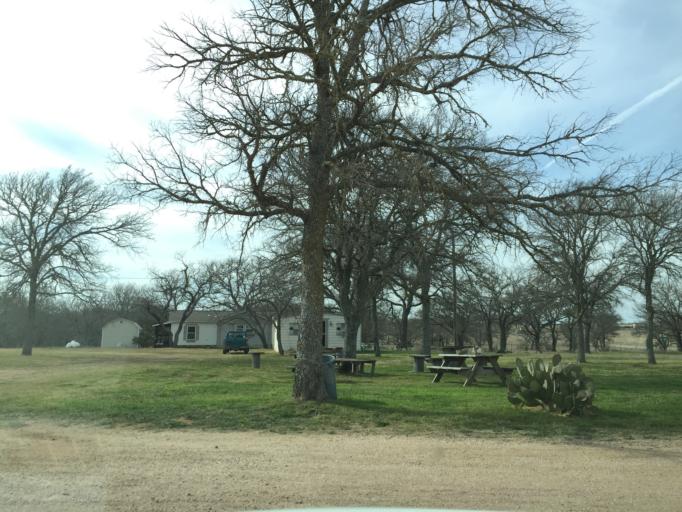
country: US
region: Texas
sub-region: Gillespie County
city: Fredericksburg
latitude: 30.4118
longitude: -98.7332
